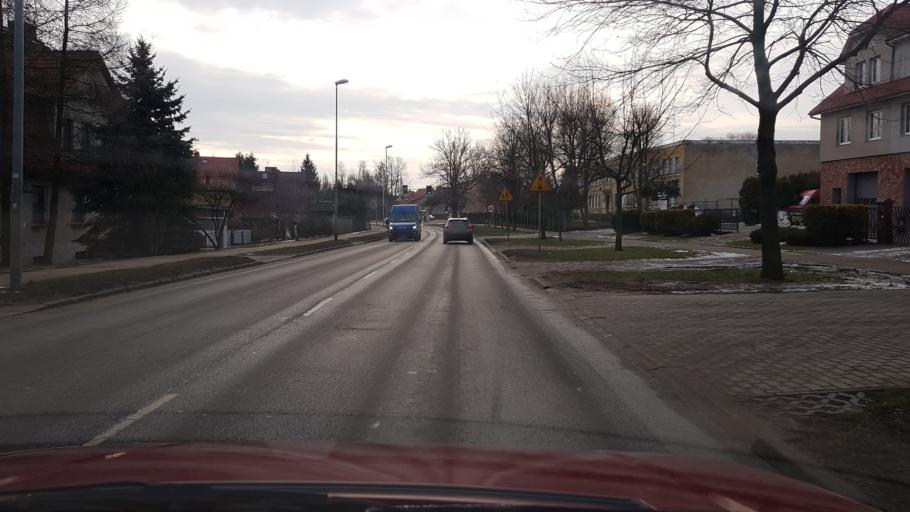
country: PL
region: West Pomeranian Voivodeship
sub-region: Szczecin
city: Szczecin
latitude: 53.4778
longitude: 14.5882
